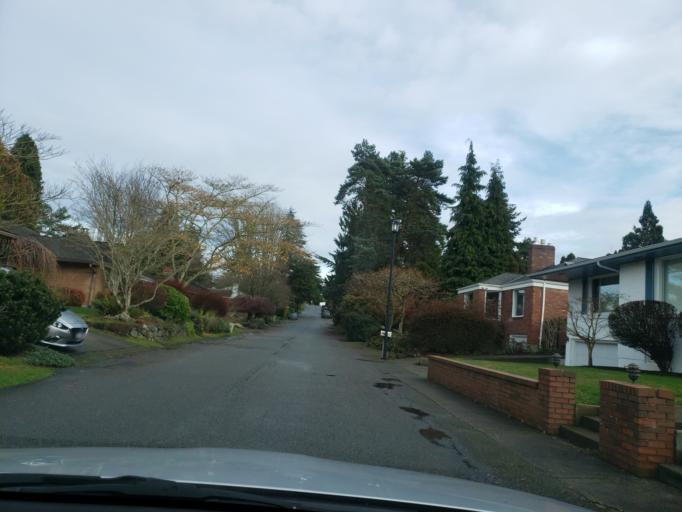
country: US
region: Washington
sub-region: King County
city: Shoreline
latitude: 47.7016
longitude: -122.3794
